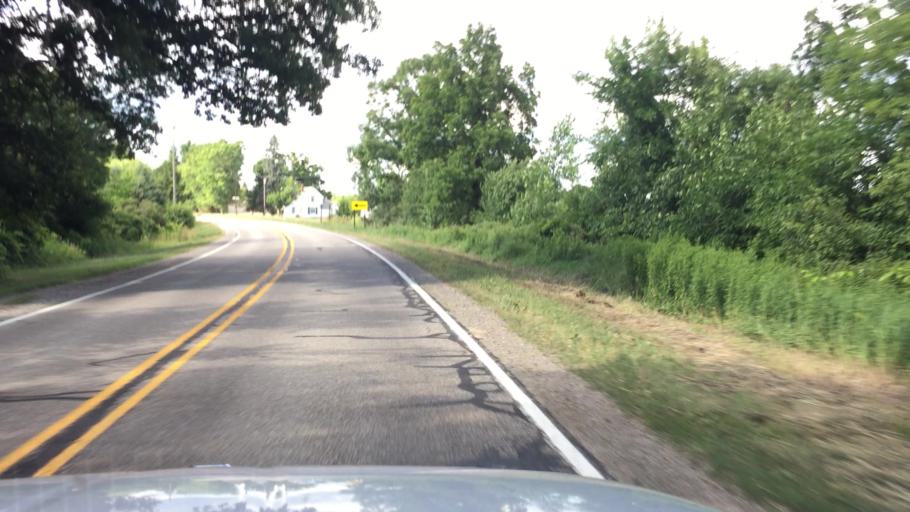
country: US
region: Michigan
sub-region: Saint Clair County
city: Capac
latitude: 43.0918
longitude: -82.9095
